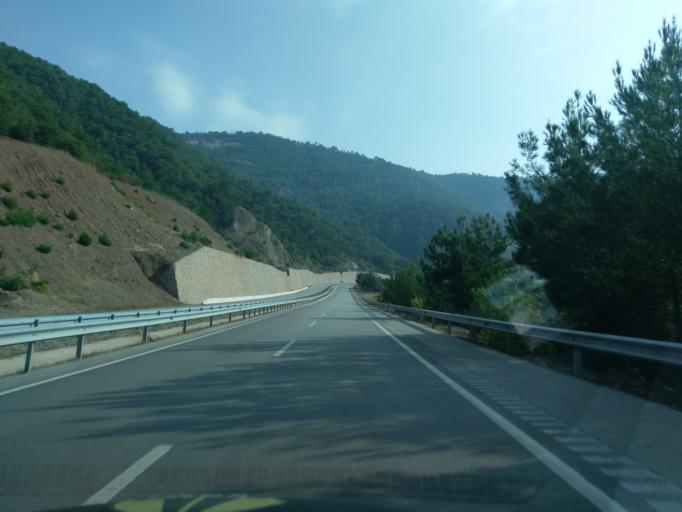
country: TR
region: Amasya
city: Akdag
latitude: 40.7521
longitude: 36.0798
